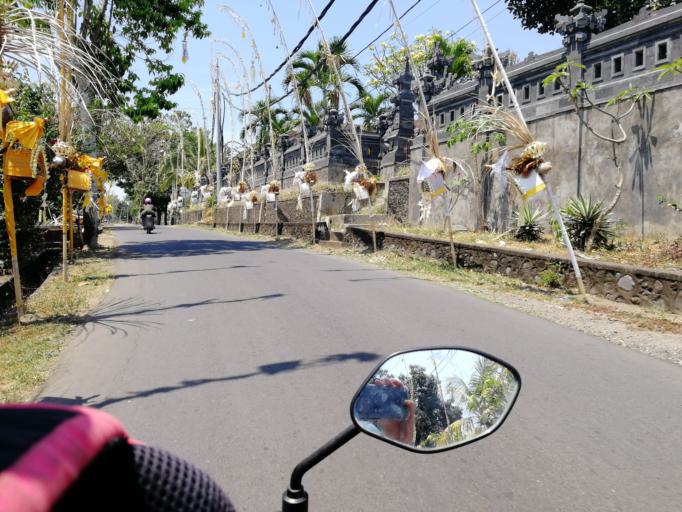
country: ID
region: Bali
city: Banjar Timbrah
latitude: -8.4701
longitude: 115.5917
